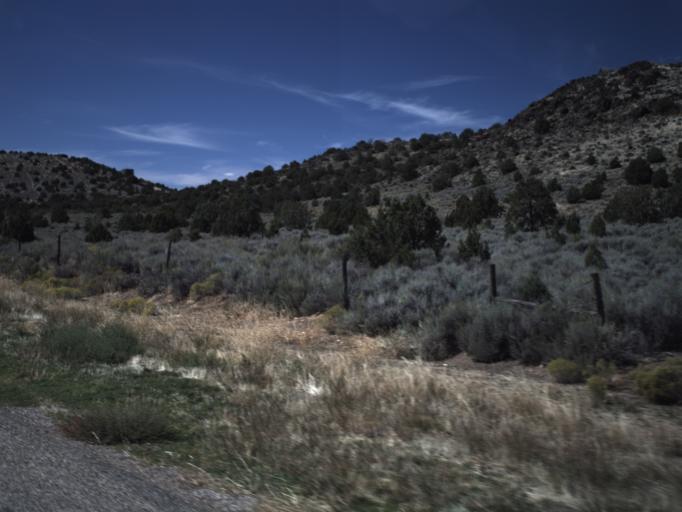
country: US
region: Utah
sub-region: Washington County
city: Ivins
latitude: 37.3710
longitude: -113.6627
